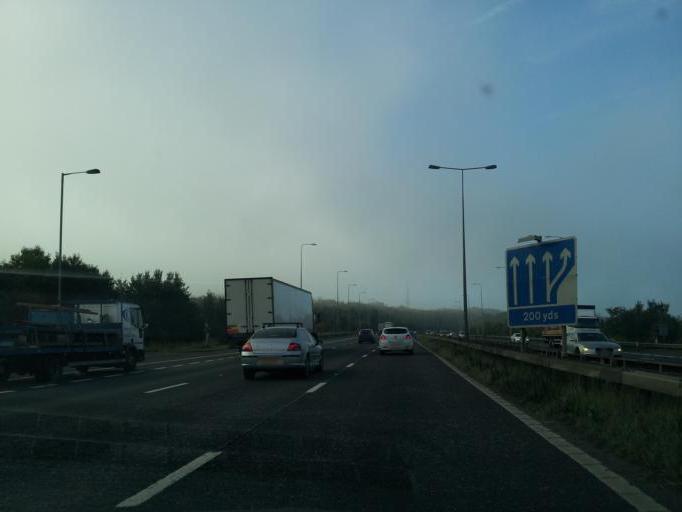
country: GB
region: England
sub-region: Calderdale
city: Brighouse
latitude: 53.6912
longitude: -1.7577
